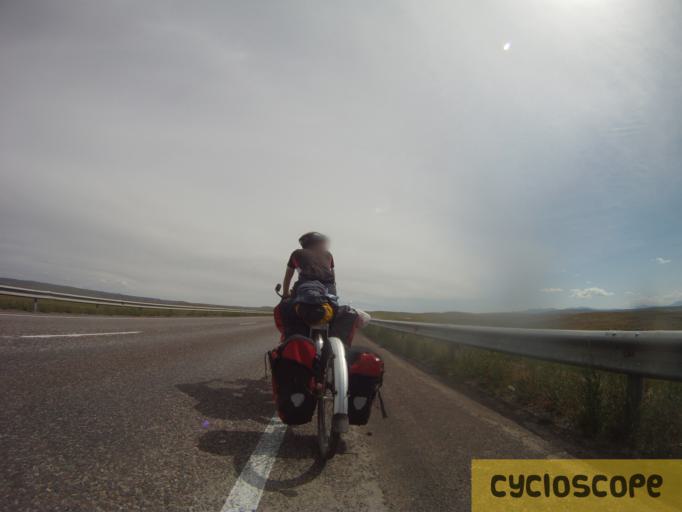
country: KZ
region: Zhambyl
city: Georgiyevka
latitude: 43.2804
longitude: 74.8521
